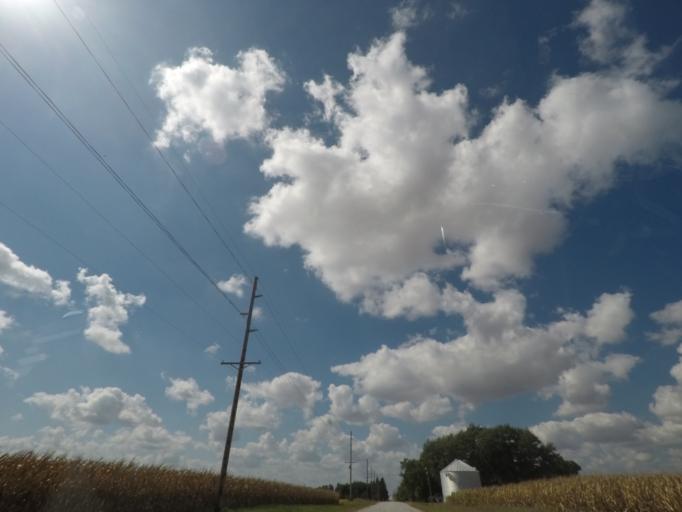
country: US
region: Iowa
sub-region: Story County
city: Nevada
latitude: 42.0344
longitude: -93.3901
